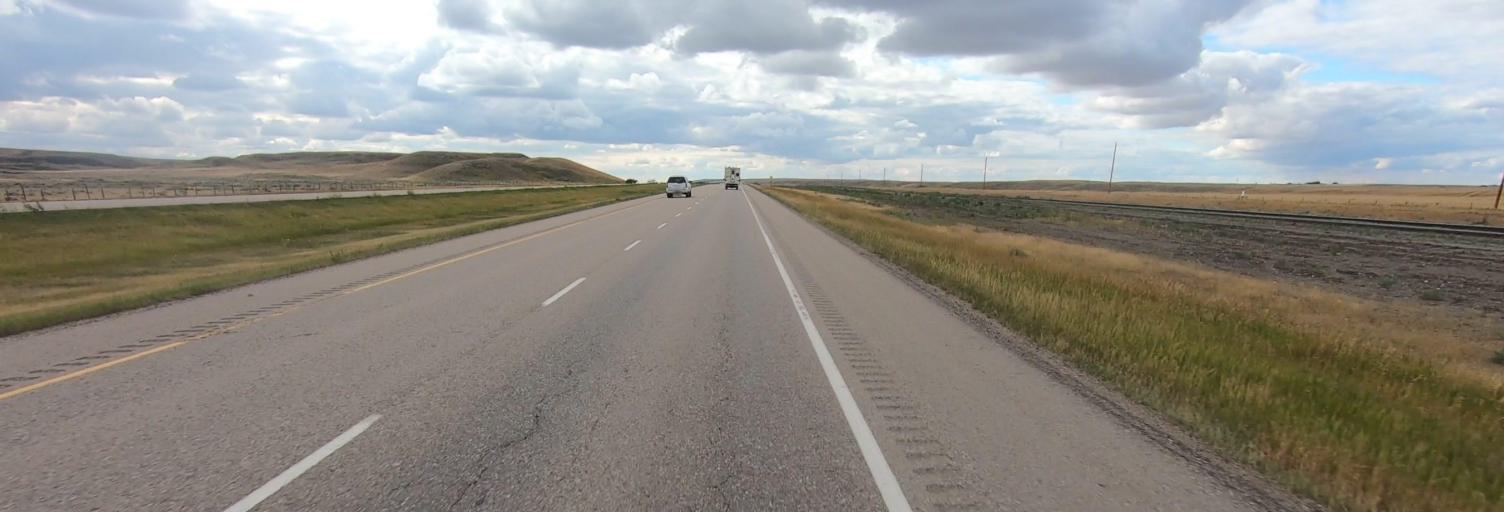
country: CA
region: Alberta
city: Medicine Hat
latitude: 49.9492
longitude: -110.2224
